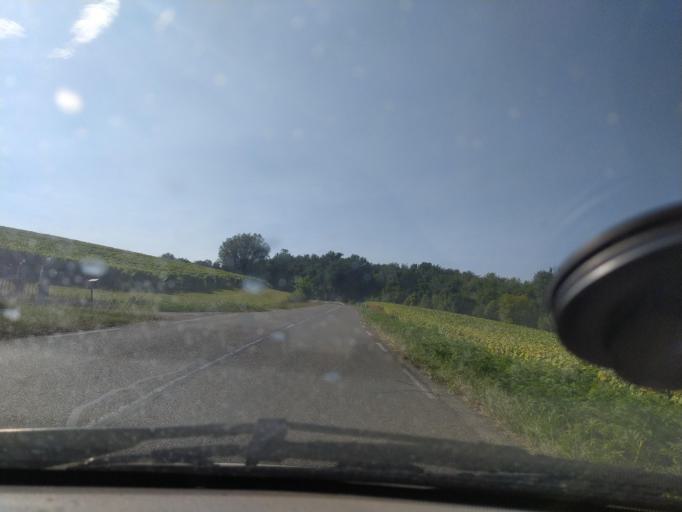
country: FR
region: Midi-Pyrenees
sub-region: Departement du Gers
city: Nogaro
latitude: 43.7939
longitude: 0.0253
